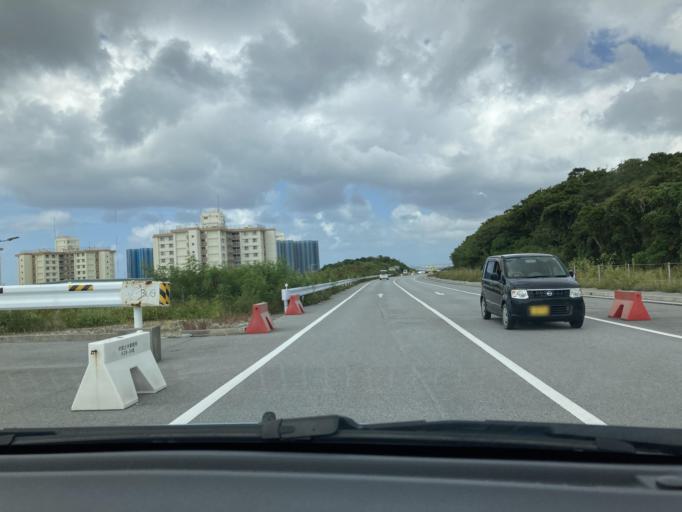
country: JP
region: Okinawa
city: Ginowan
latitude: 26.2644
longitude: 127.7087
